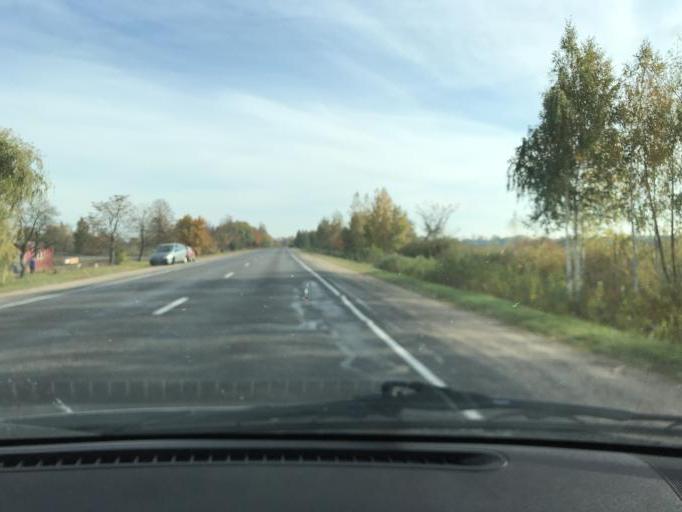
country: BY
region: Brest
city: Asnyezhytsy
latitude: 52.2035
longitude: 26.0587
